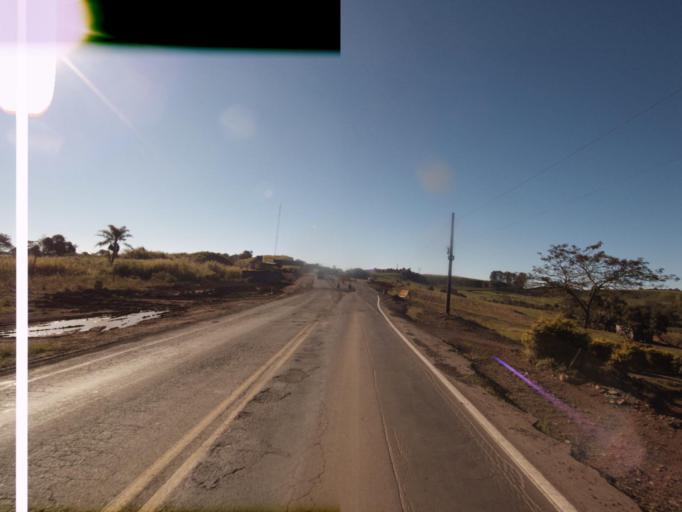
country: AR
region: Misiones
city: Bernardo de Irigoyen
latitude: -26.6401
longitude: -53.5183
